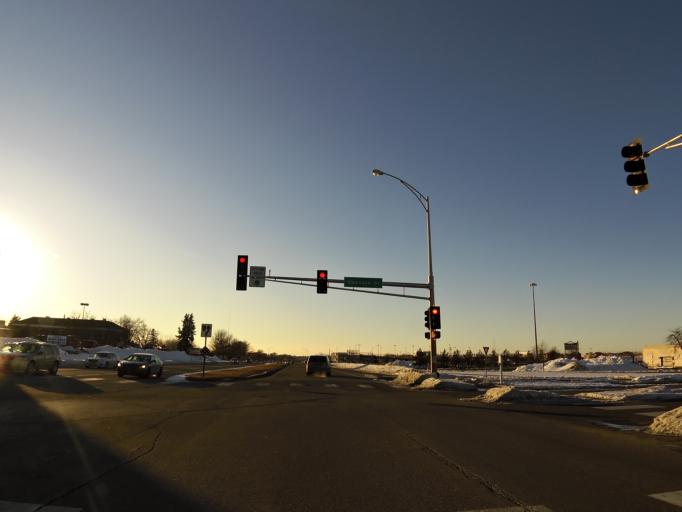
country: US
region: Minnesota
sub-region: Ramsey County
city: North Saint Paul
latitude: 45.0280
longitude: -93.0205
